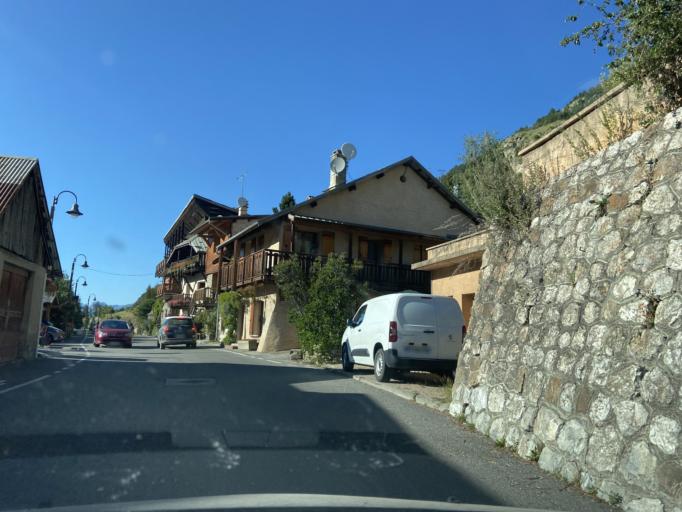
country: FR
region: Provence-Alpes-Cote d'Azur
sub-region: Departement des Hautes-Alpes
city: Guillestre
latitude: 44.6103
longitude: 6.6881
